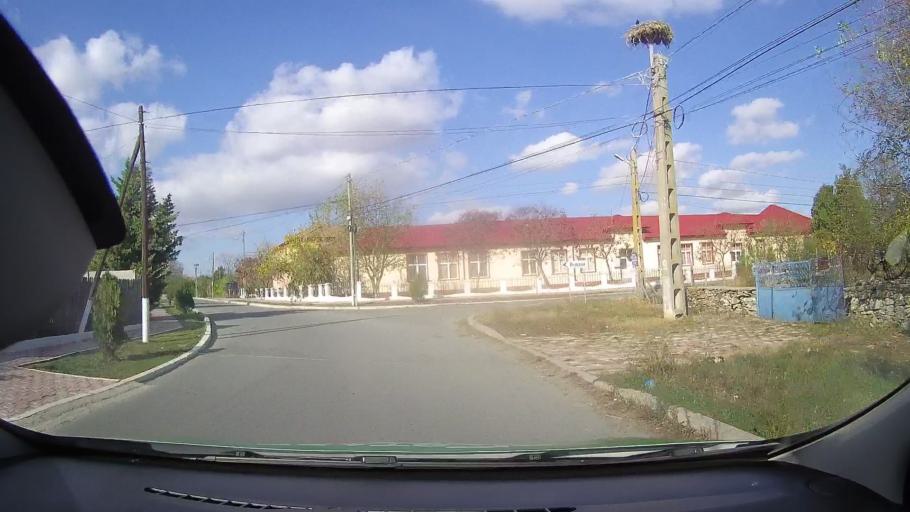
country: RO
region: Constanta
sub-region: Comuna Istria
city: Istria
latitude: 44.5723
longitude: 28.7121
